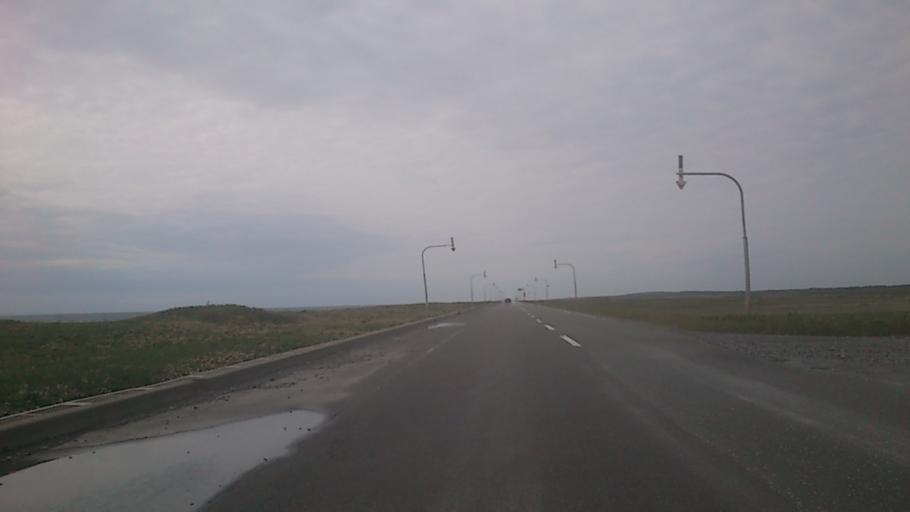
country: JP
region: Hokkaido
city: Makubetsu
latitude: 45.0240
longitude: 141.6690
